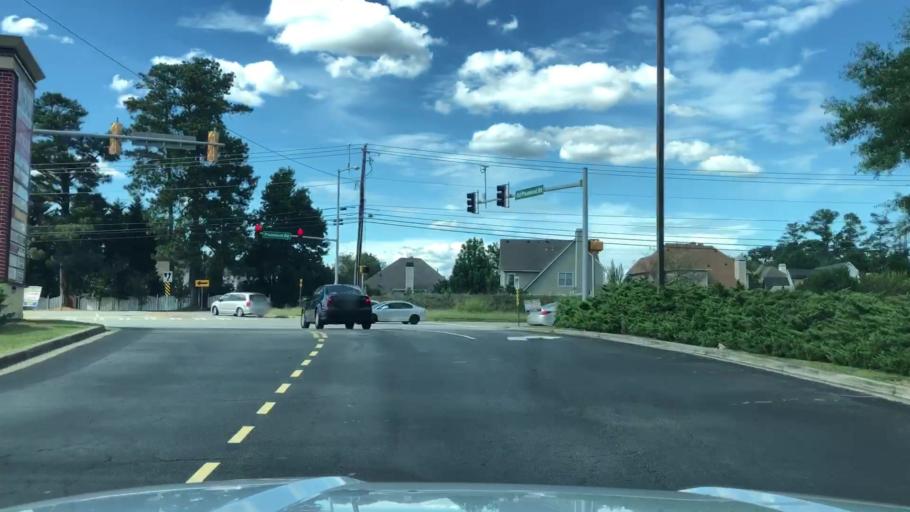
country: US
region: Georgia
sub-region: Cobb County
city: Marietta
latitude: 34.0199
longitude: -84.5258
